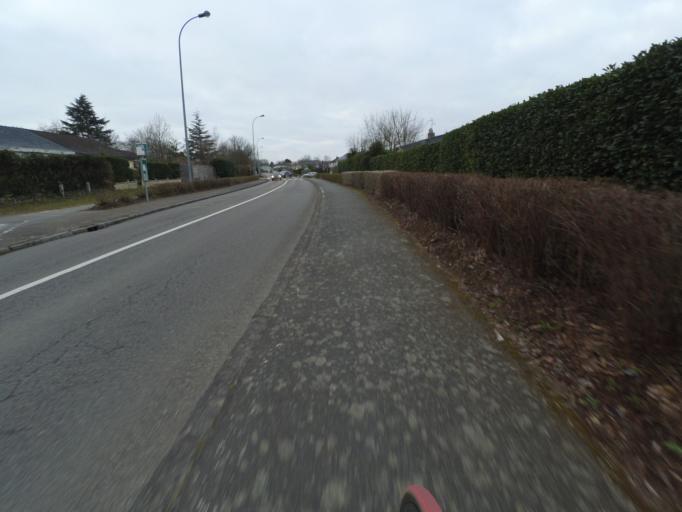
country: FR
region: Pays de la Loire
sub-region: Departement de la Loire-Atlantique
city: Carquefou
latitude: 47.2807
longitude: -1.4855
